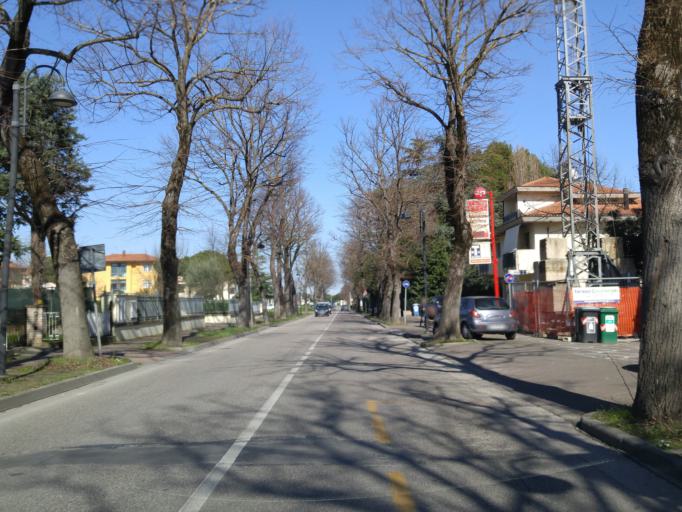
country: IT
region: Emilia-Romagna
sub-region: Provincia di Rimini
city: San Giovanni in Marignano
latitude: 43.9413
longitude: 12.7161
